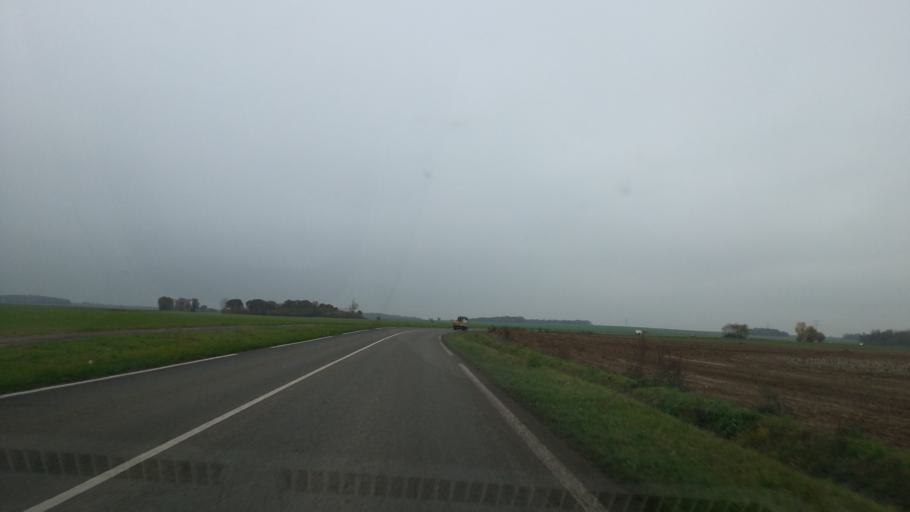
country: FR
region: Picardie
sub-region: Departement de l'Oise
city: Boran-sur-Oise
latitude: 49.1639
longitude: 2.3435
